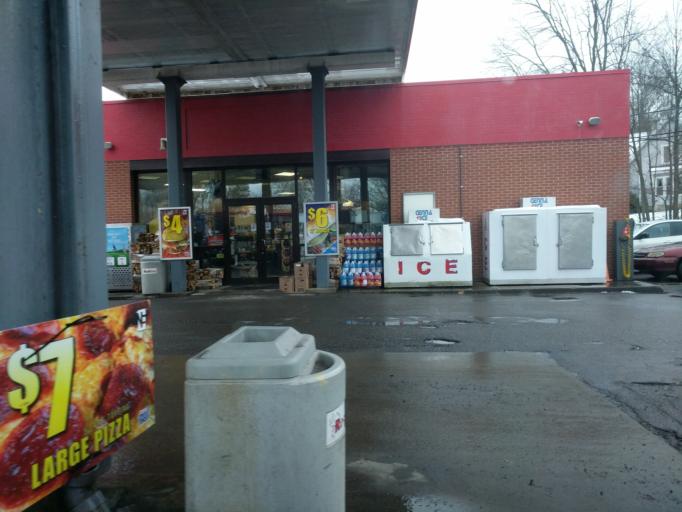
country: US
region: Pennsylvania
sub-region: Tioga County
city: Wellsboro
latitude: 41.7519
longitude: -77.2976
